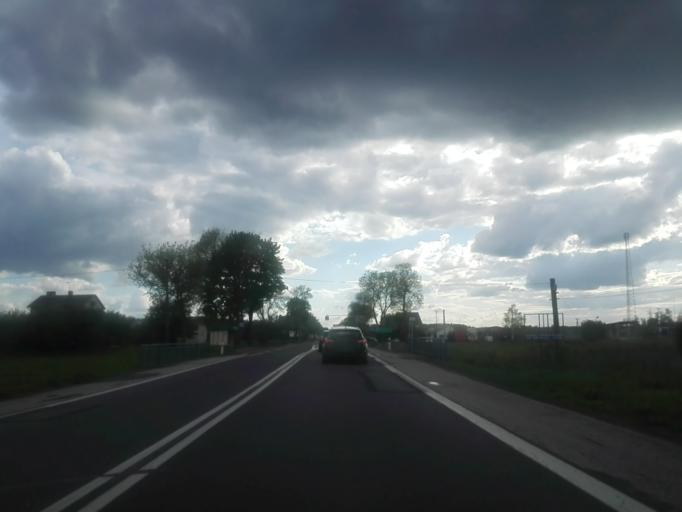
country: PL
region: Masovian Voivodeship
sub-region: Powiat ostrowski
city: Brok
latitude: 52.7579
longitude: 21.7972
